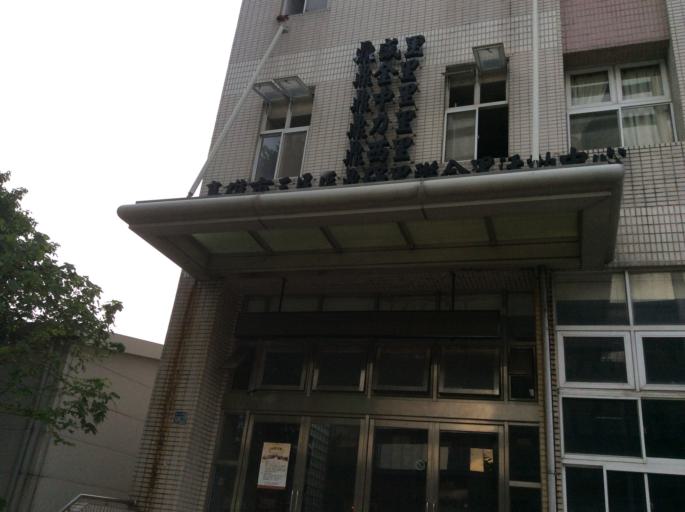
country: TW
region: Kaohsiung
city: Kaohsiung
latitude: 22.6666
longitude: 120.3220
